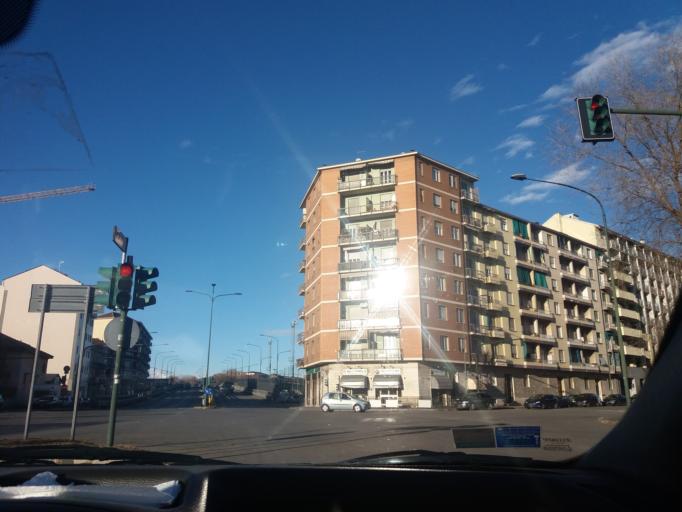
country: IT
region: Piedmont
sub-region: Provincia di Torino
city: Lesna
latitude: 45.0537
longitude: 7.6300
